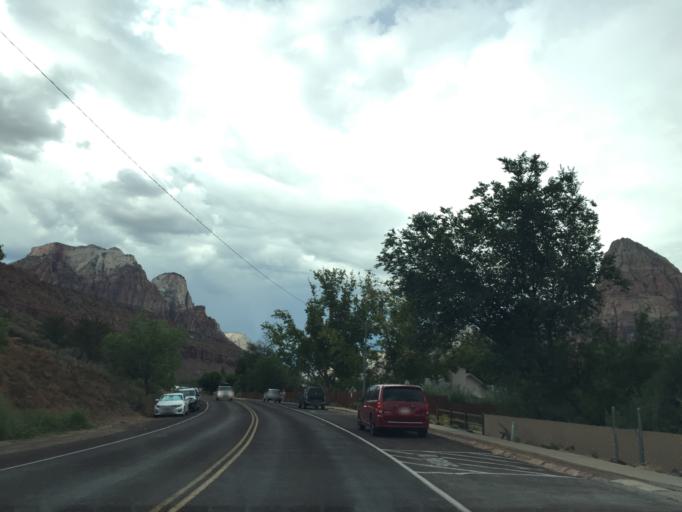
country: US
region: Utah
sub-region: Washington County
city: Hildale
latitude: 37.1918
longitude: -112.9940
